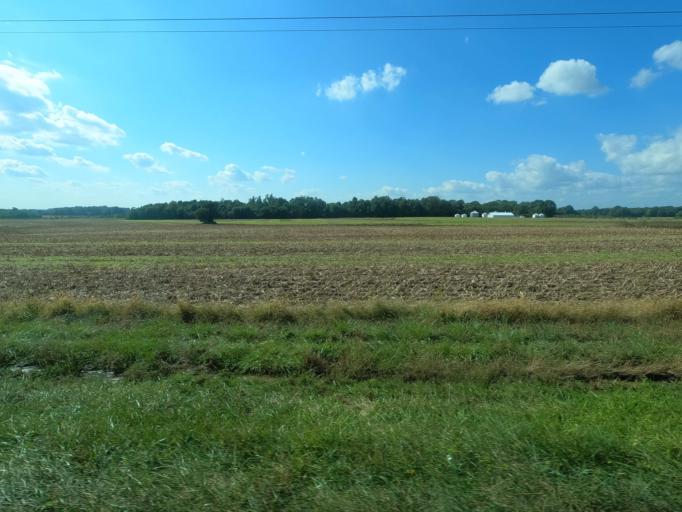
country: US
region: Illinois
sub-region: Massac County
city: Metropolis
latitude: 37.2141
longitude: -88.7290
